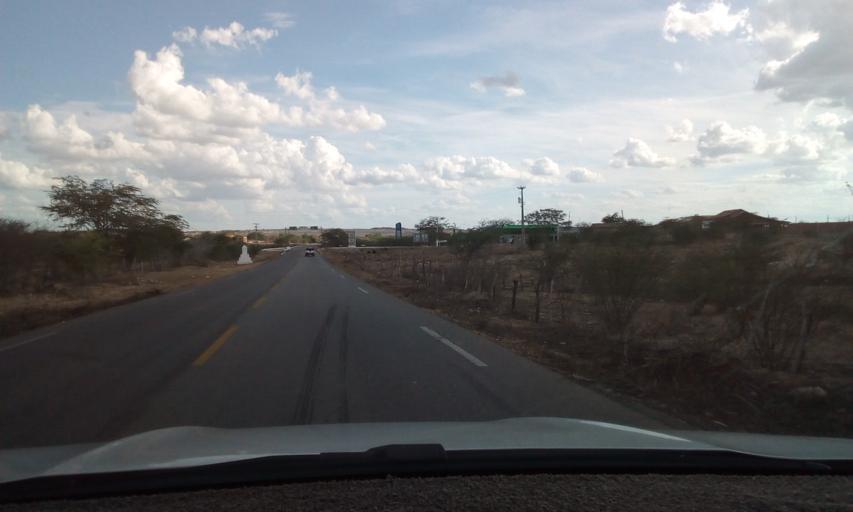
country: BR
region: Paraiba
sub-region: Soledade
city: Soledade
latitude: -6.9359
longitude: -36.3860
